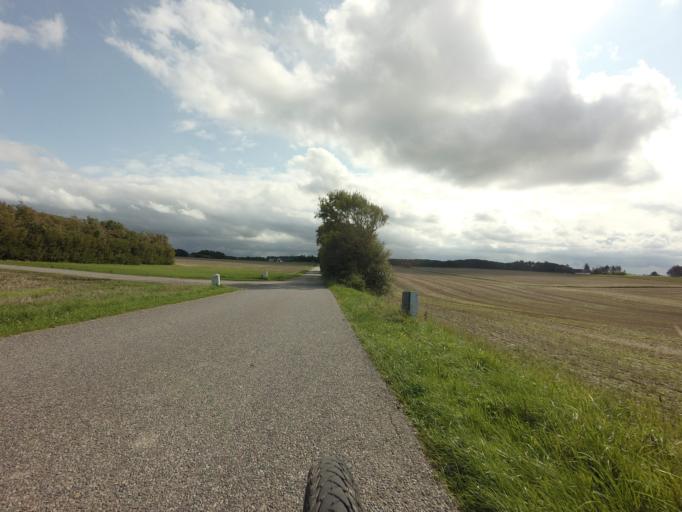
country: DK
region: North Denmark
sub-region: Hjorring Kommune
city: Hjorring
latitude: 57.5235
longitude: 10.0466
